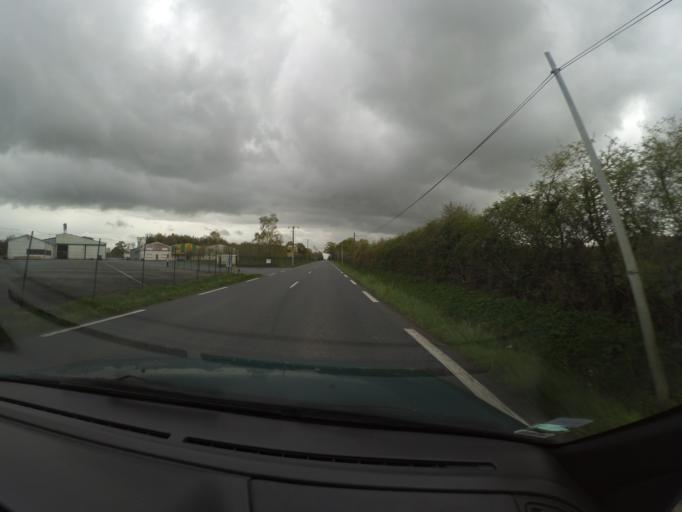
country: FR
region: Pays de la Loire
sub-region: Departement de la Loire-Atlantique
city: La Remaudiere
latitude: 47.2132
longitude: -1.2384
